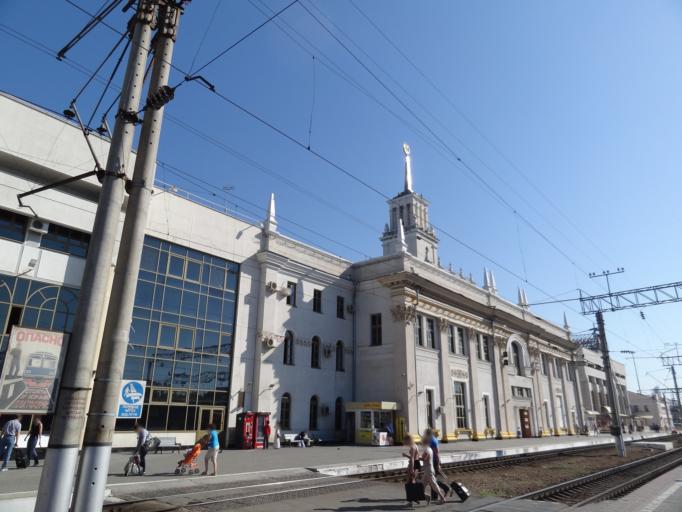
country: RU
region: Krasnodarskiy
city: Krasnodar
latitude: 45.0179
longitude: 38.9881
